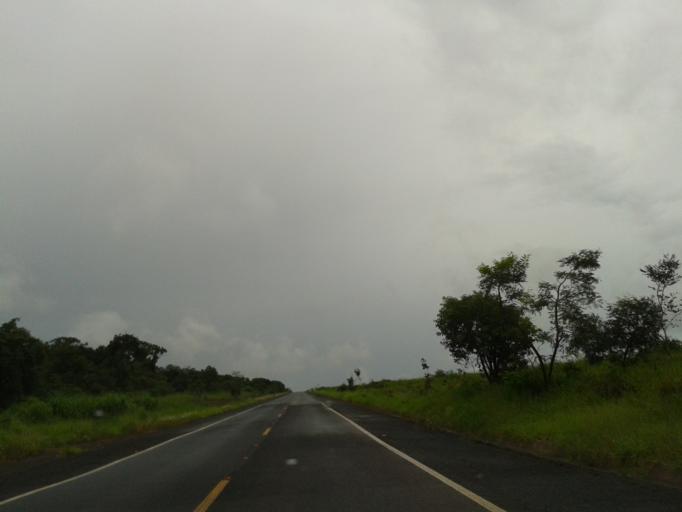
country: BR
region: Minas Gerais
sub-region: Santa Vitoria
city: Santa Vitoria
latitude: -19.1498
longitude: -50.1575
